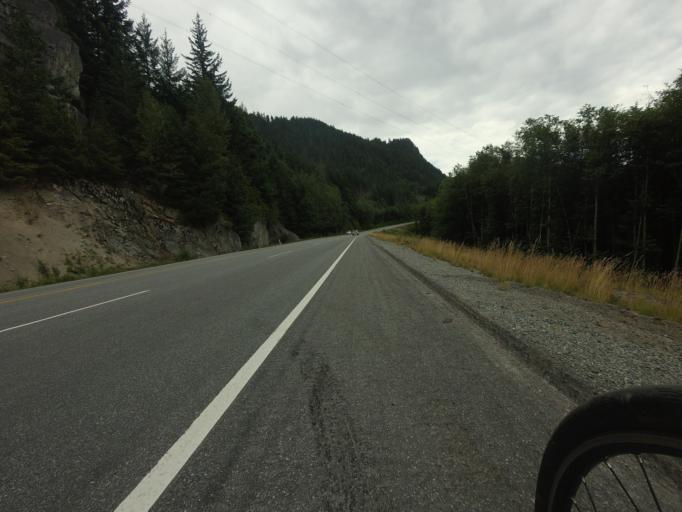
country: CA
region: British Columbia
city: Whistler
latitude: 49.8393
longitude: -123.1380
